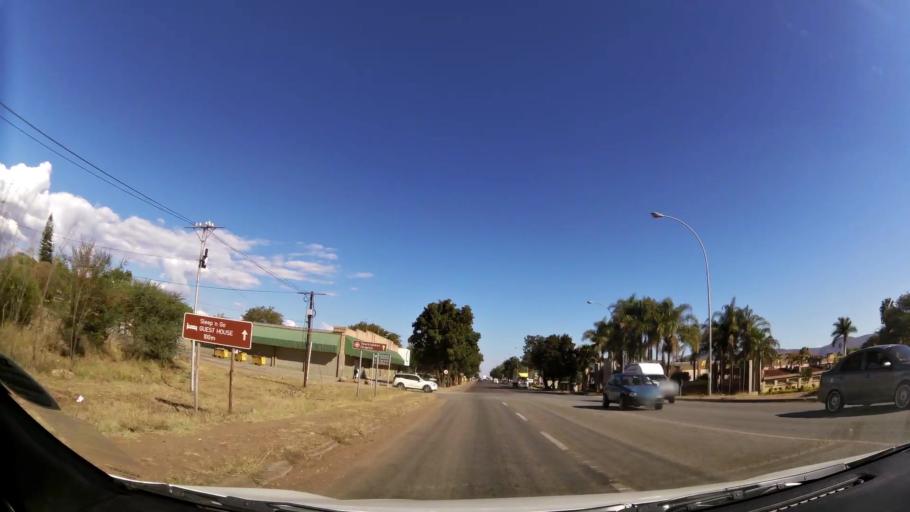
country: ZA
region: Limpopo
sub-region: Waterberg District Municipality
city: Mokopane
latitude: -24.1745
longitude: 29.0163
